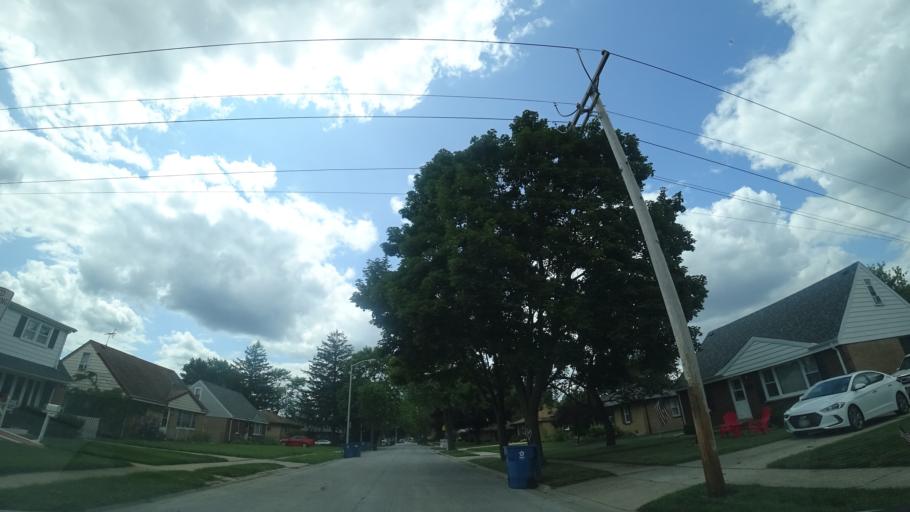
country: US
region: Illinois
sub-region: Cook County
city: Alsip
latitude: 41.6806
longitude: -87.7294
